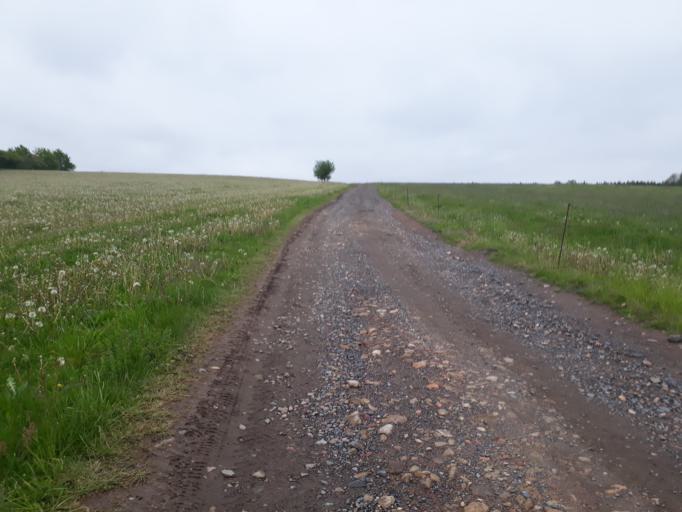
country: DE
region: Saxony
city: Reinhardtsgrimma
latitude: 50.8876
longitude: 13.7534
